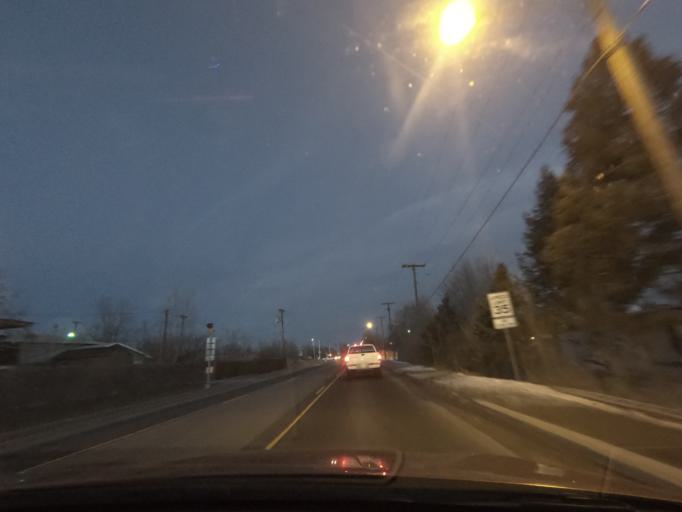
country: US
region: Colorado
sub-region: El Paso County
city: Security-Widefield
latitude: 38.7373
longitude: -104.7208
